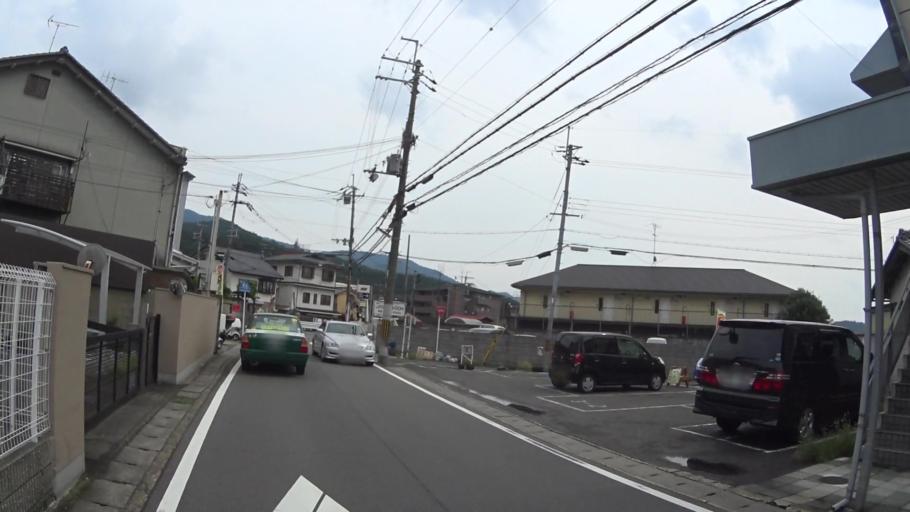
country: JP
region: Kyoto
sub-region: Kyoto-shi
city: Kamigyo-ku
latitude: 35.0723
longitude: 135.7922
